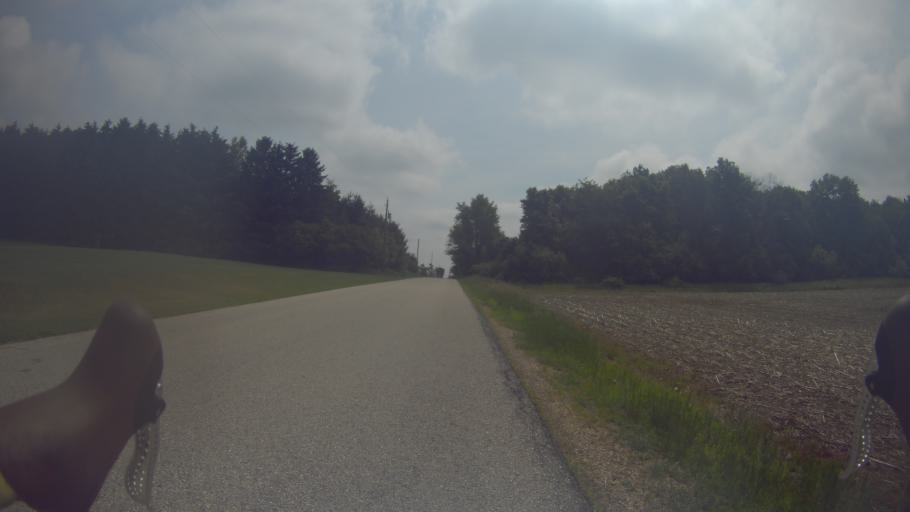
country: US
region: Wisconsin
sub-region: Jefferson County
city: Cambridge
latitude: 42.9237
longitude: -89.0101
